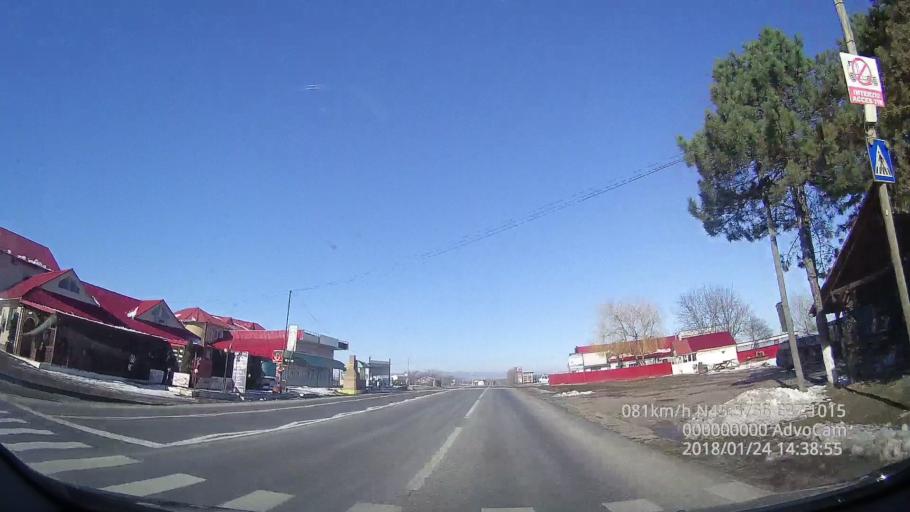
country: RO
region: Vrancea
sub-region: Comuna Popesti
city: Popesti
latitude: 45.5760
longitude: 27.1012
